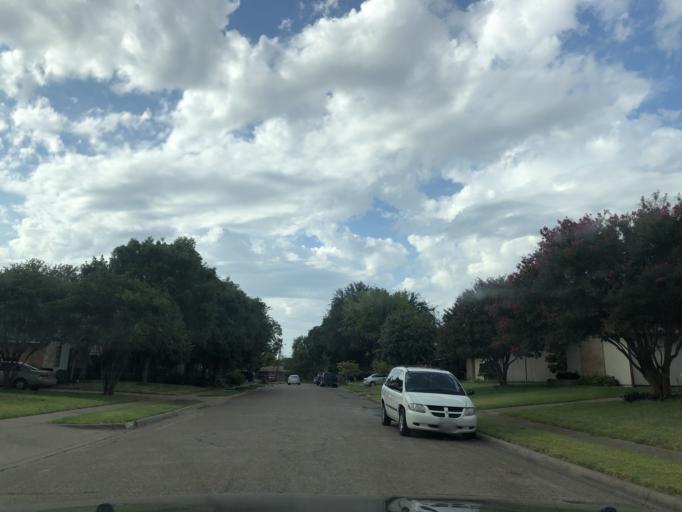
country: US
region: Texas
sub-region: Dallas County
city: Garland
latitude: 32.8897
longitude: -96.6639
